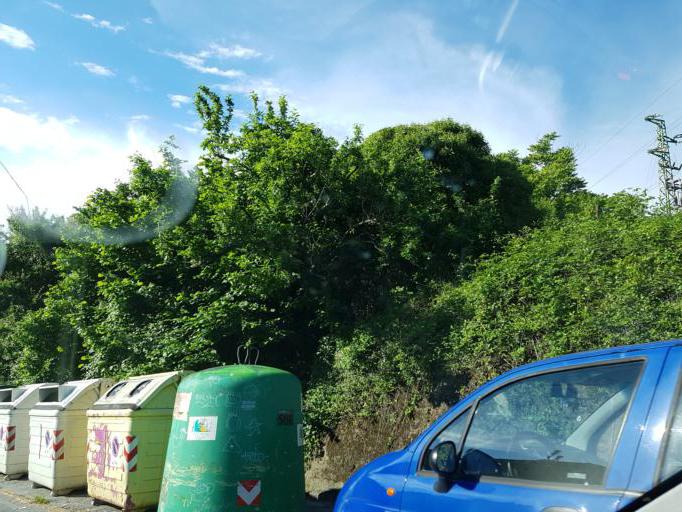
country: IT
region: Liguria
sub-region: Provincia di Genova
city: Manesseno
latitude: 44.4749
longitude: 8.9160
